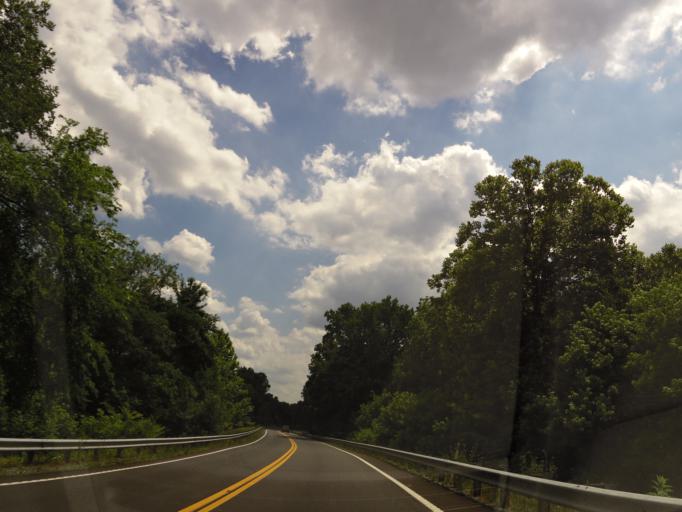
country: US
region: Tennessee
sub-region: Sequatchie County
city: Dunlap
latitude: 35.4635
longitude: -85.3265
